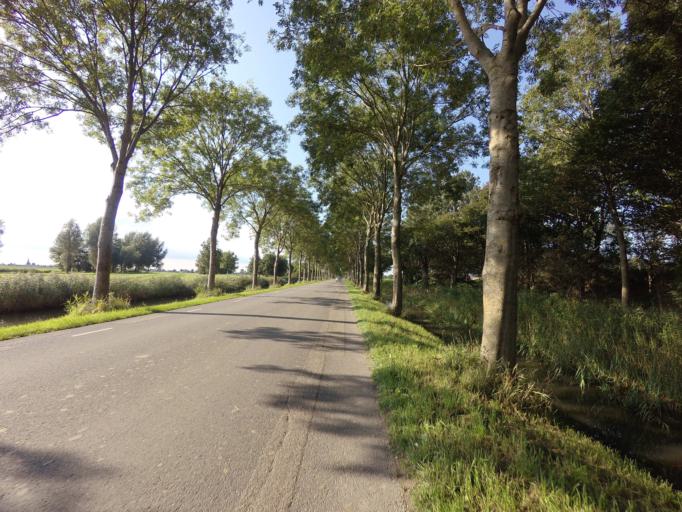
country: NL
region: North Holland
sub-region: Gemeente Hoorn
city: Hoorn
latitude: 52.6676
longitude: 5.1442
